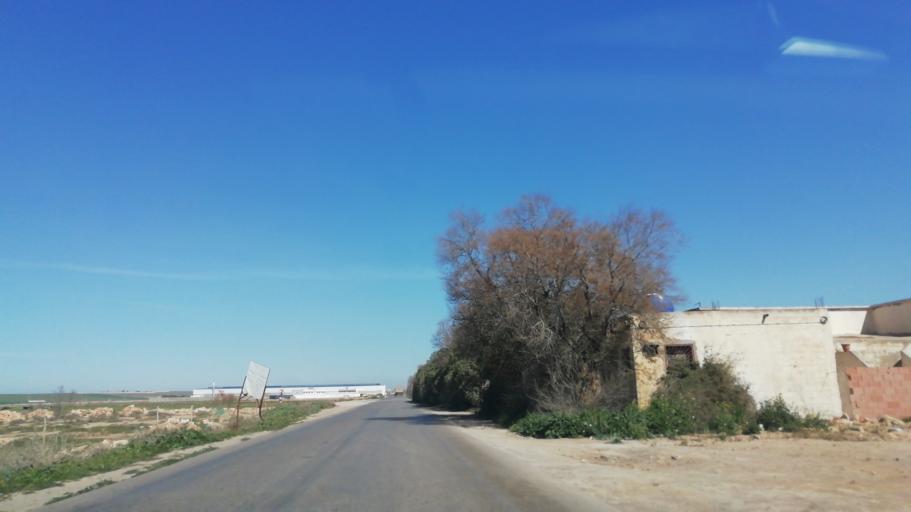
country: DZ
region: Oran
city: Es Senia
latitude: 35.5029
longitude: -0.5943
